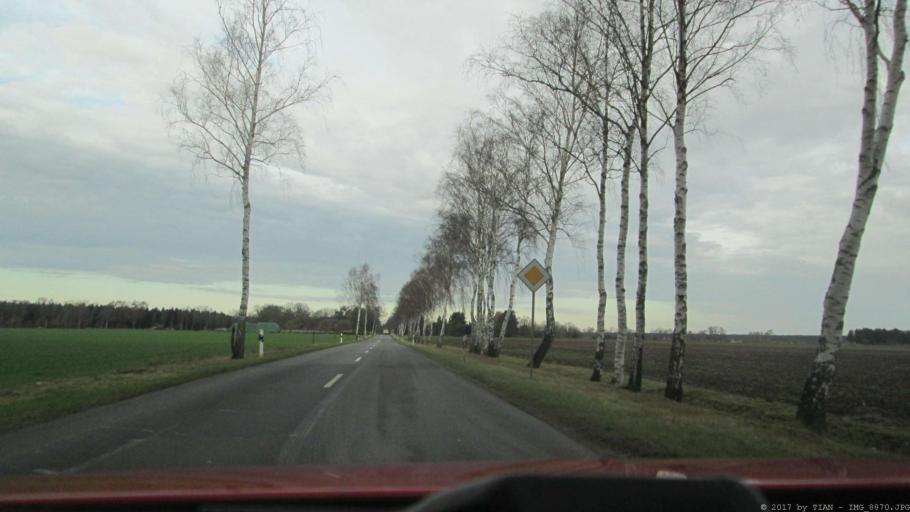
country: DE
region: Lower Saxony
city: Bokensdorf
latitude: 52.5354
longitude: 10.7235
